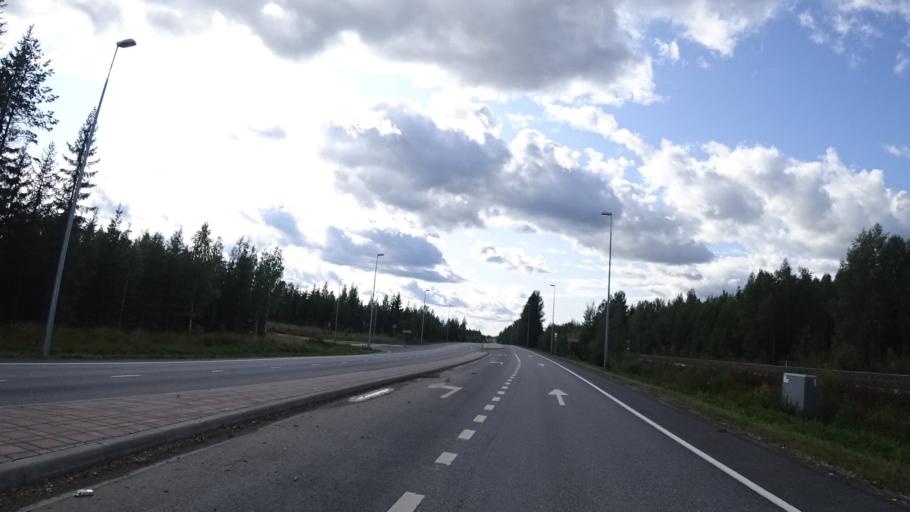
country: RU
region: Republic of Karelia
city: Vyartsilya
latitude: 62.1766
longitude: 30.5813
